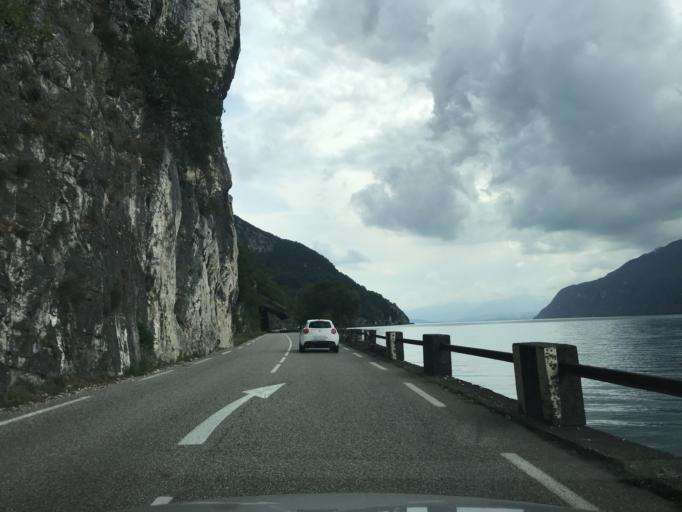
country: FR
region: Rhone-Alpes
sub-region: Departement de la Savoie
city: Chatillon
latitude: 45.7721
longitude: 5.8681
